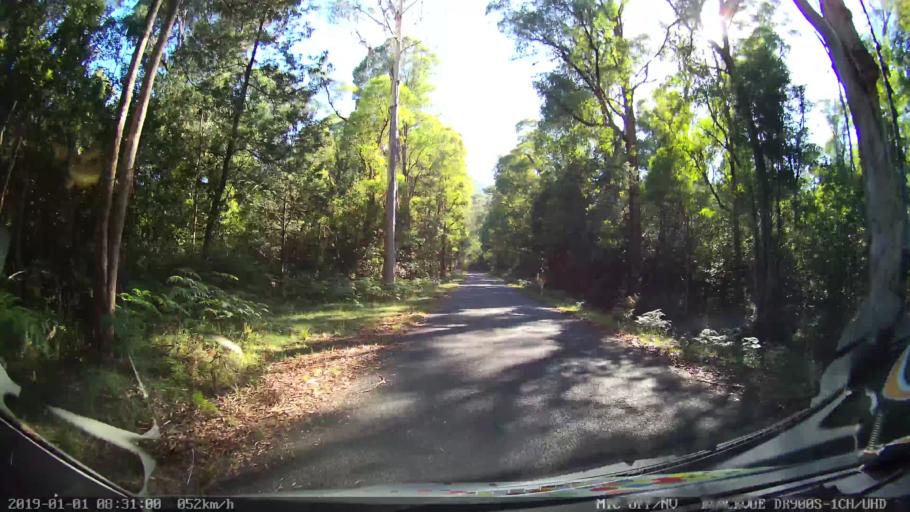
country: AU
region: New South Wales
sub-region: Snowy River
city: Jindabyne
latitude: -36.3726
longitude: 148.2022
